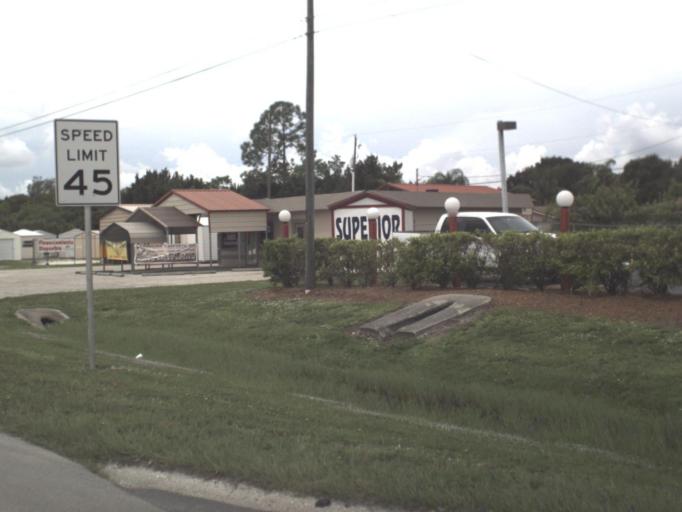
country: US
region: Florida
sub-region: Lee County
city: Fort Myers Shores
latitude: 26.7080
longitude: -81.7304
